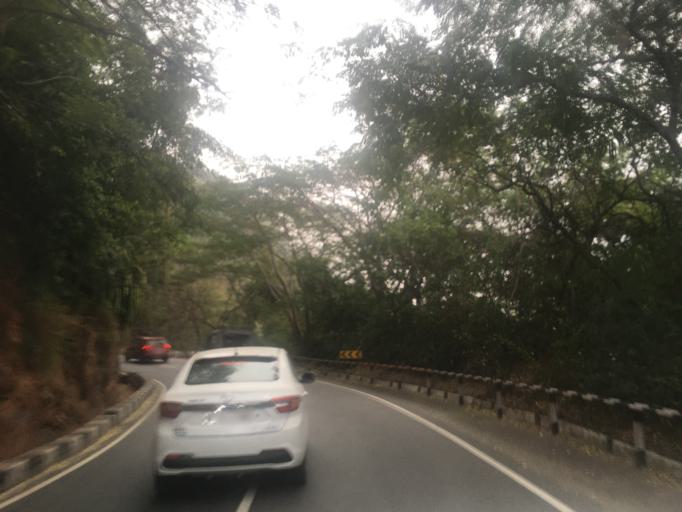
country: IN
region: Andhra Pradesh
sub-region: Chittoor
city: Tirumala
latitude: 13.6678
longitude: 79.3478
